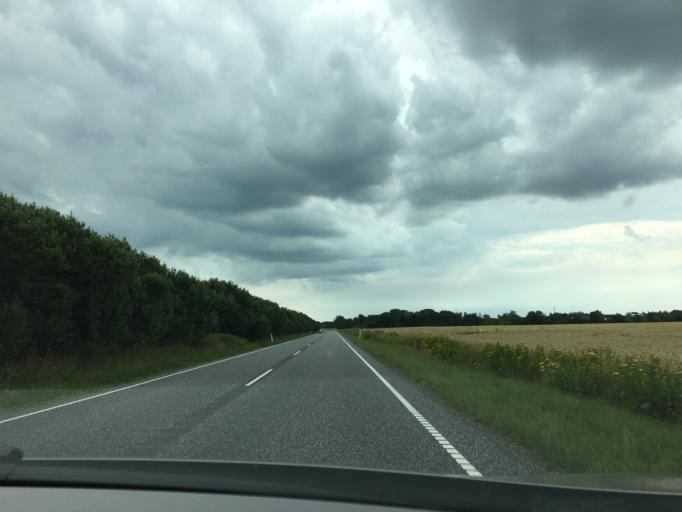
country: DK
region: Central Jutland
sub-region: Ringkobing-Skjern Kommune
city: Skjern
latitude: 55.8603
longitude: 8.3824
